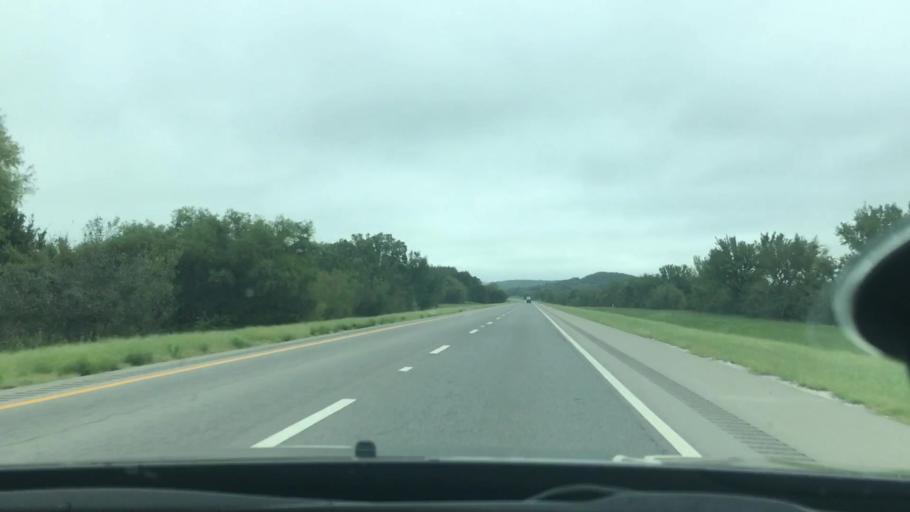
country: US
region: Oklahoma
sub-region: McIntosh County
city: Checotah
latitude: 35.4567
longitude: -95.4144
